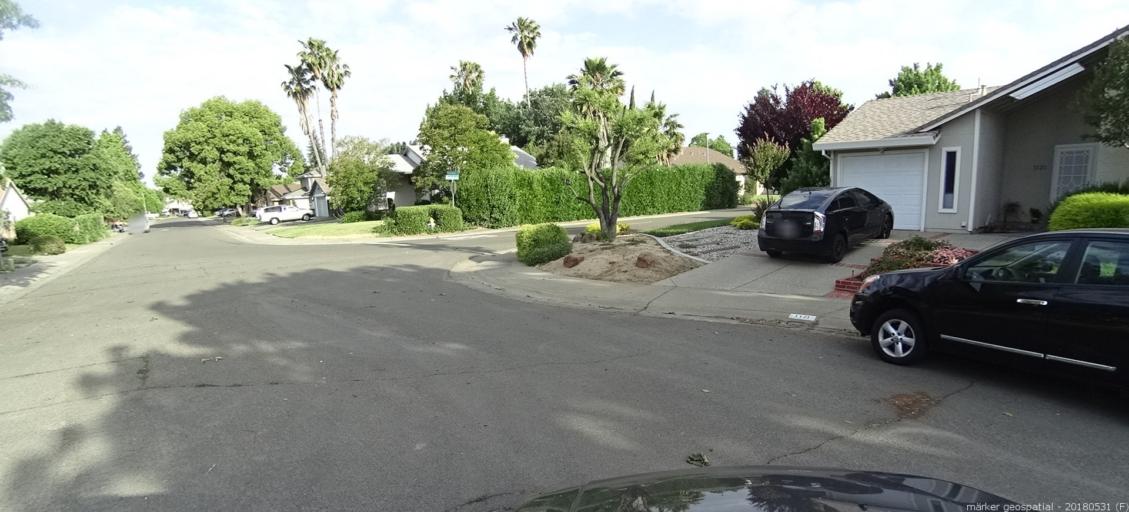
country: US
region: California
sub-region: Sacramento County
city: Sacramento
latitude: 38.6226
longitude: -121.4848
